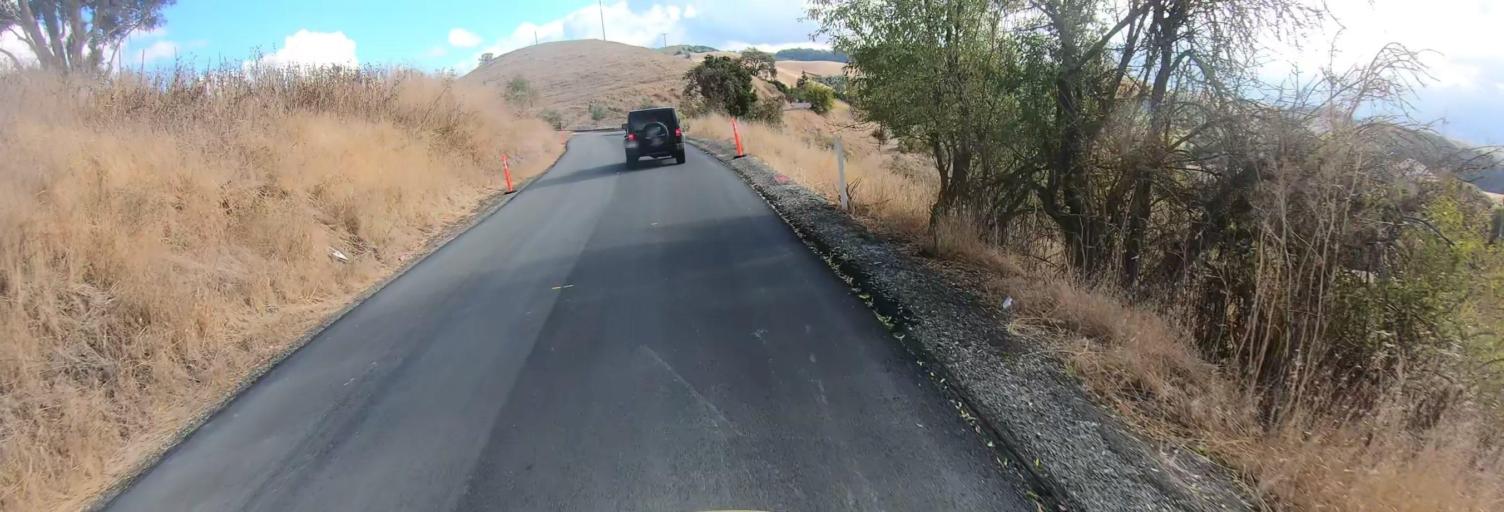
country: US
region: California
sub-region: Santa Clara County
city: East Foothills
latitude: 37.3673
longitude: -121.7660
